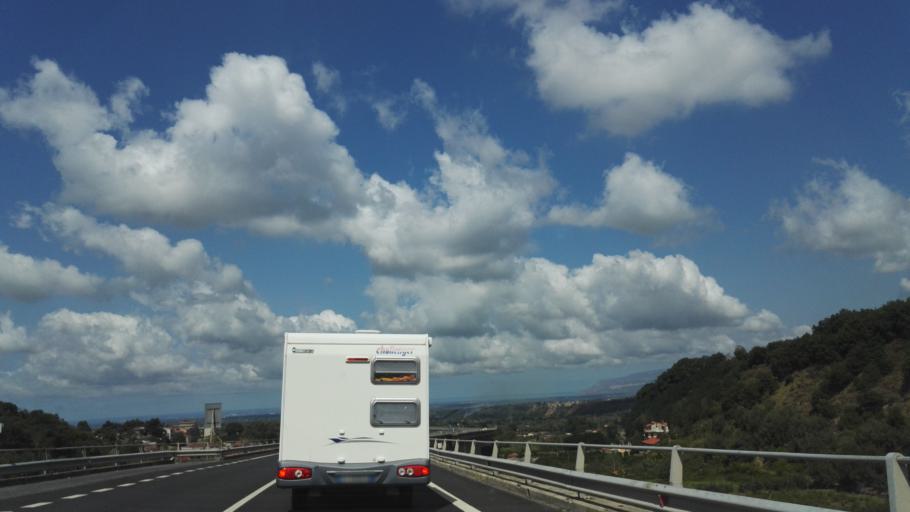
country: IT
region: Calabria
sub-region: Provincia di Reggio Calabria
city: Anoia Superiore
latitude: 38.4174
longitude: 16.1052
